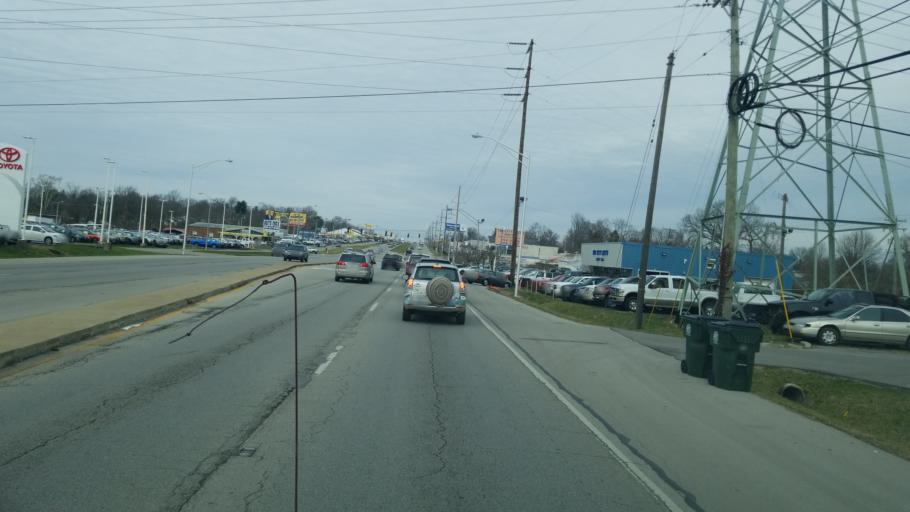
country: US
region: Kentucky
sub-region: Fayette County
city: Lexington-Fayette
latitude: 38.0505
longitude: -84.4556
